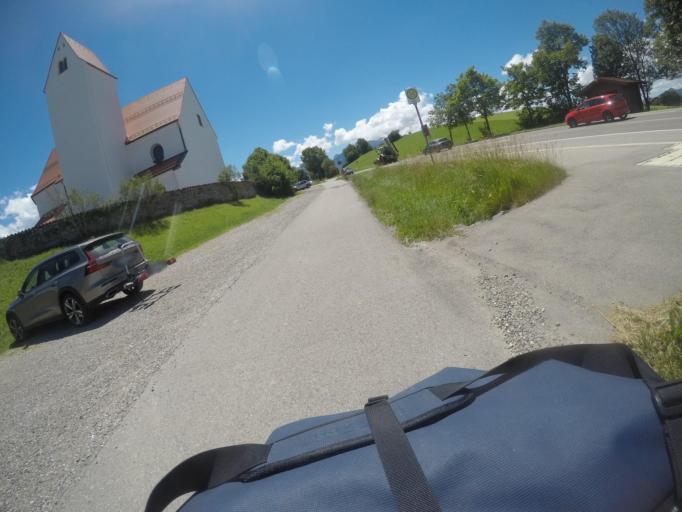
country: DE
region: Bavaria
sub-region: Swabia
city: Fuessen
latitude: 47.6081
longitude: 10.7105
